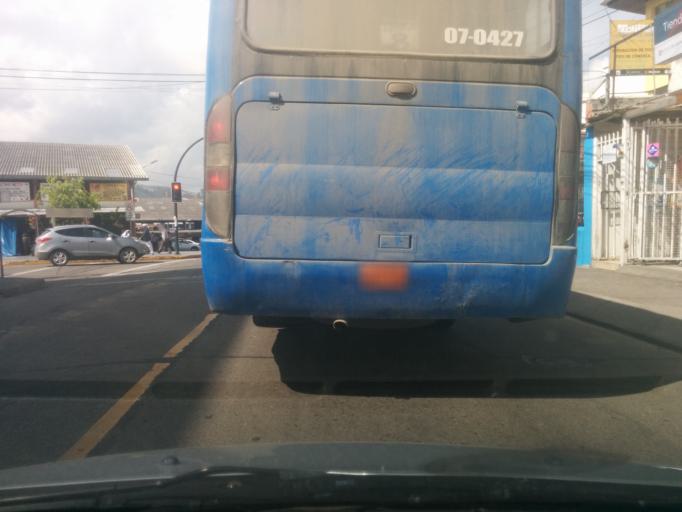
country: EC
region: Azuay
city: Cuenca
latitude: -2.9016
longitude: -78.9922
